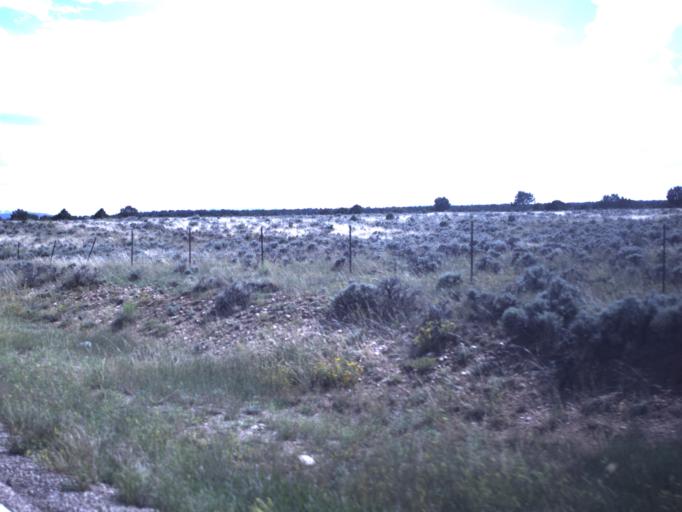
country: US
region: Utah
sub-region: Duchesne County
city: Duchesne
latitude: 40.3037
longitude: -110.6970
